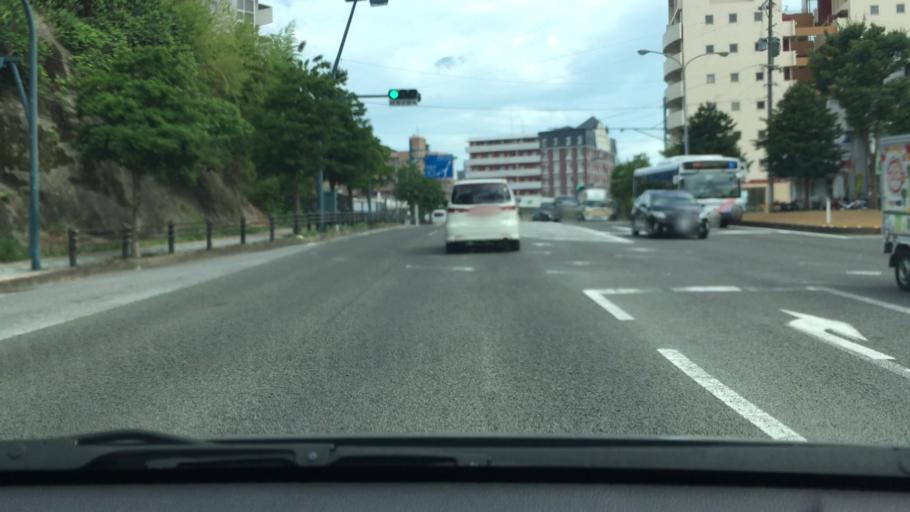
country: JP
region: Nagasaki
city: Togitsu
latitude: 32.8026
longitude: 129.8525
